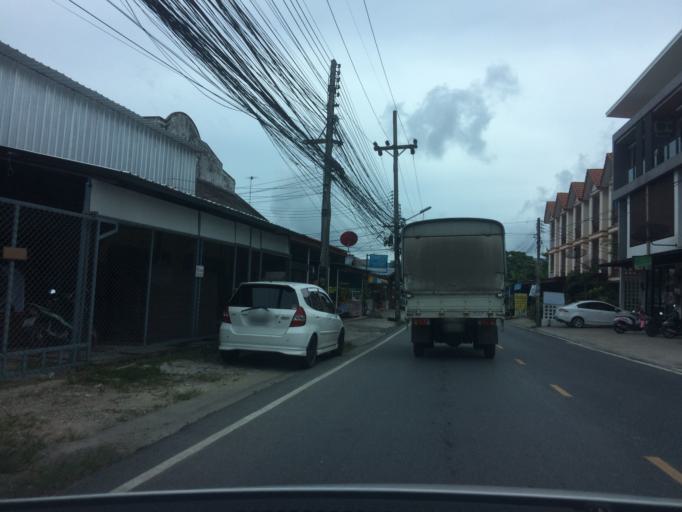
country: TH
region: Phuket
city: Mueang Phuket
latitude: 7.8622
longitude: 98.3629
